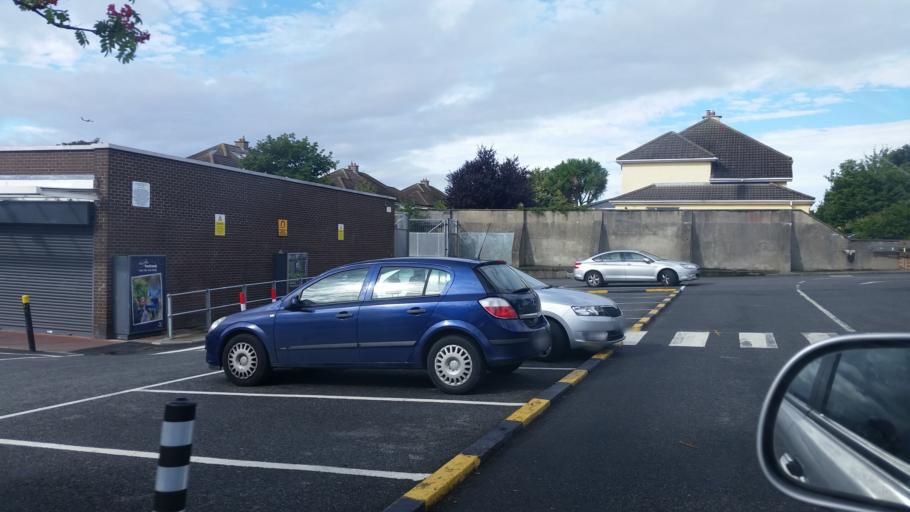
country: IE
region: Leinster
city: Portmarnock
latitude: 53.4350
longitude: -6.1306
